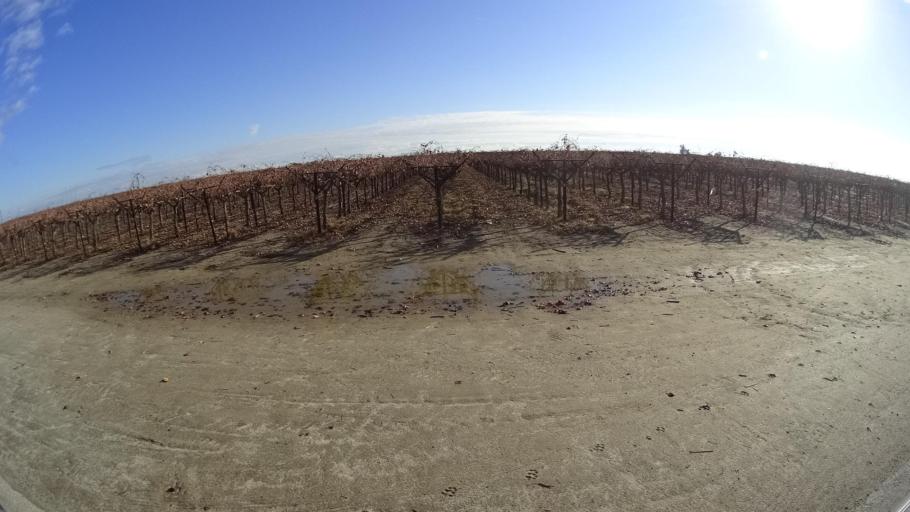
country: US
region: California
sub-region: Kern County
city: Delano
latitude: 35.7302
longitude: -119.3030
